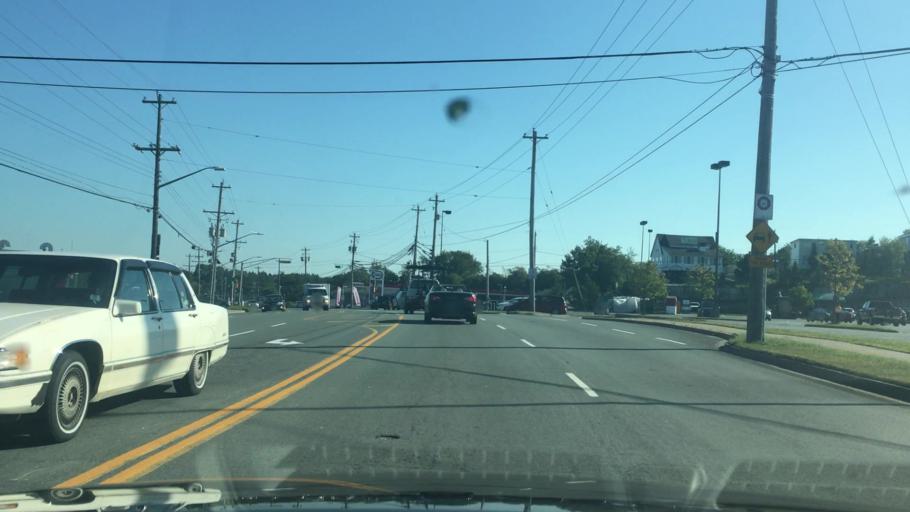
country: CA
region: Nova Scotia
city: Cole Harbour
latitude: 44.6940
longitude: -63.4985
